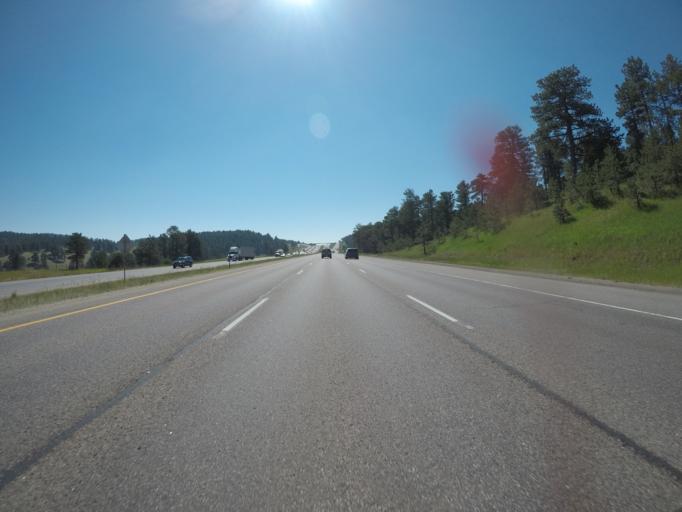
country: US
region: Colorado
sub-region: Jefferson County
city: Genesee
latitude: 39.7133
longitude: -105.3073
